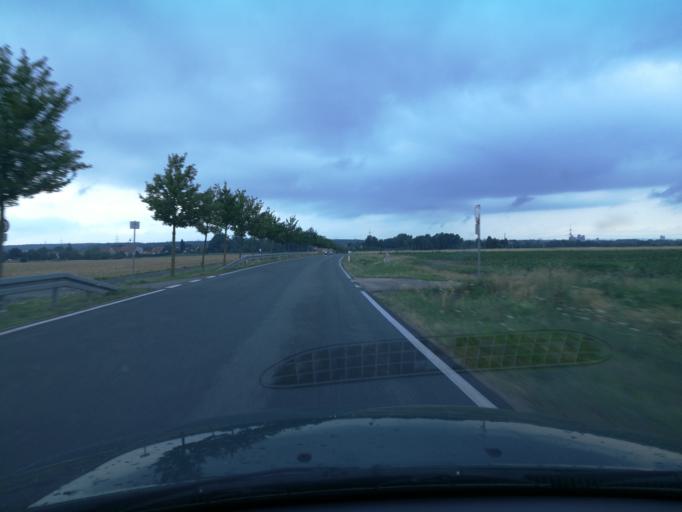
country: DE
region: Bavaria
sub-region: Regierungsbezirk Mittelfranken
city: Obermichelbach
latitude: 49.5495
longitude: 10.9601
